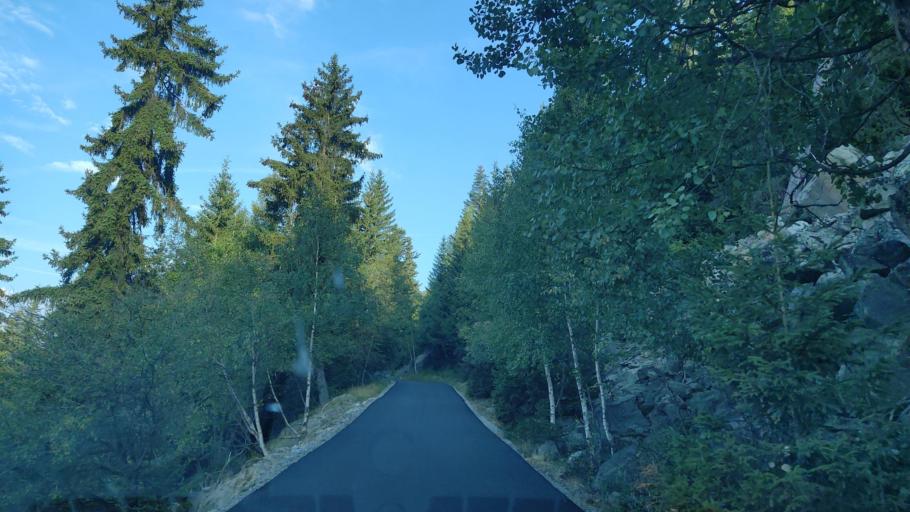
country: FR
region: Rhone-Alpes
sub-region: Departement de la Savoie
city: Val Thorens
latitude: 45.2214
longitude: 6.5613
